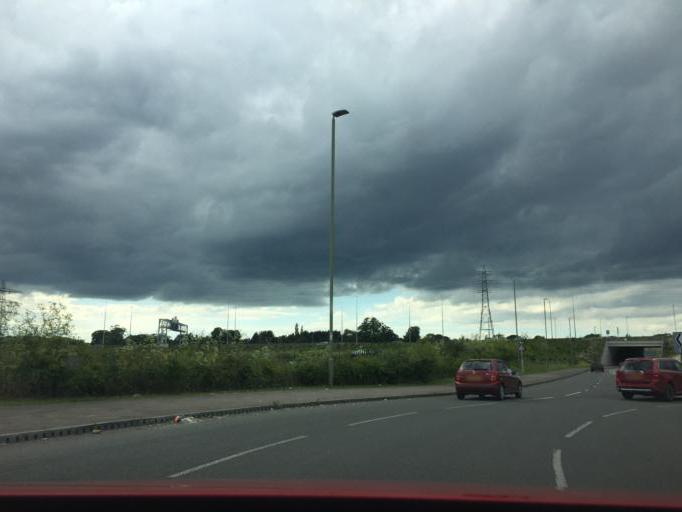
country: GB
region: England
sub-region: Luton
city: Luton
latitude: 51.8562
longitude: -0.4157
